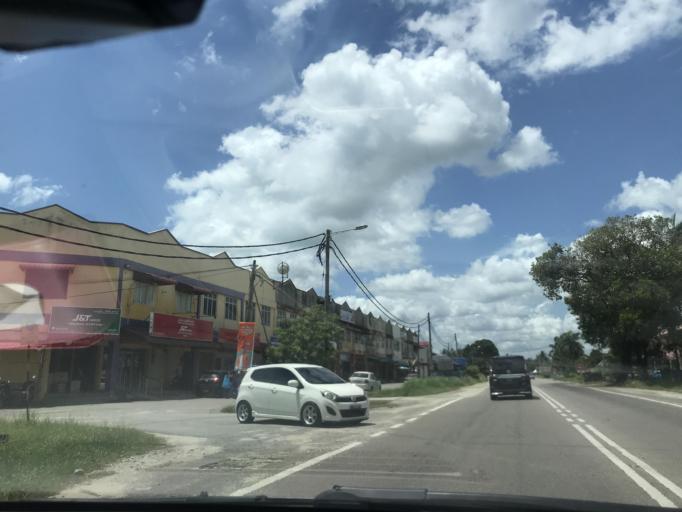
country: TH
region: Narathiwat
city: Tak Bai
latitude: 6.2287
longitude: 102.0946
